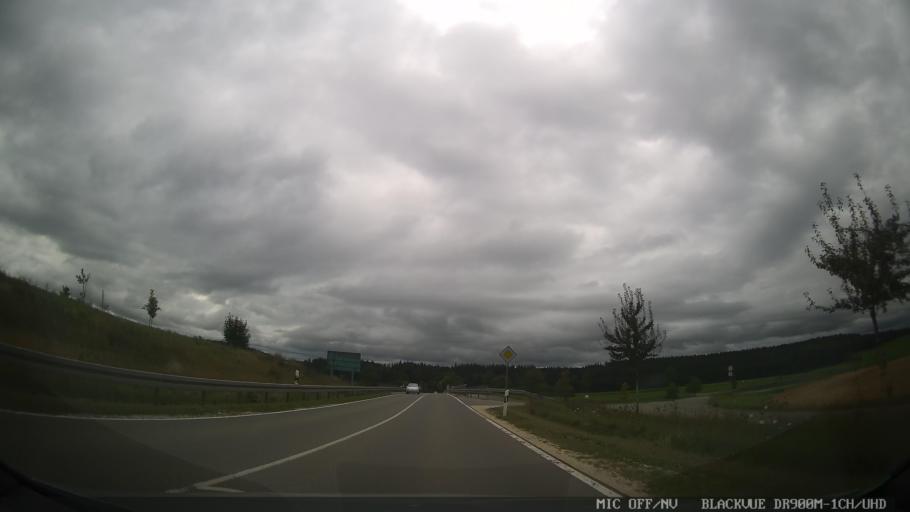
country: DE
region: Baden-Wuerttemberg
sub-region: Freiburg Region
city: Neuhausen ob Eck
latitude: 47.9641
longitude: 8.9296
